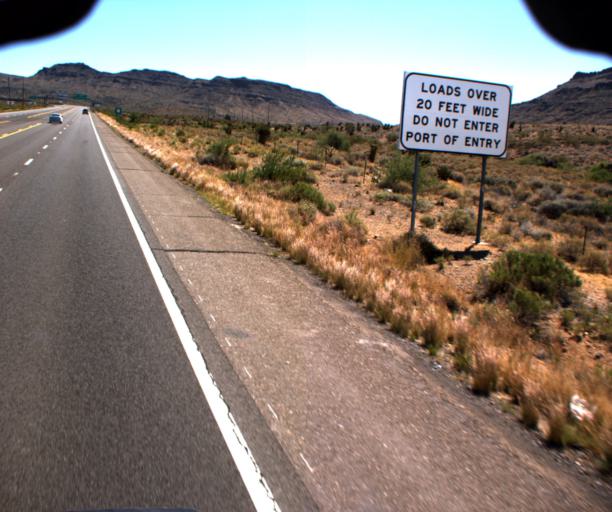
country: US
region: Arizona
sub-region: Mohave County
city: Golden Valley
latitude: 35.2188
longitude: -114.1373
